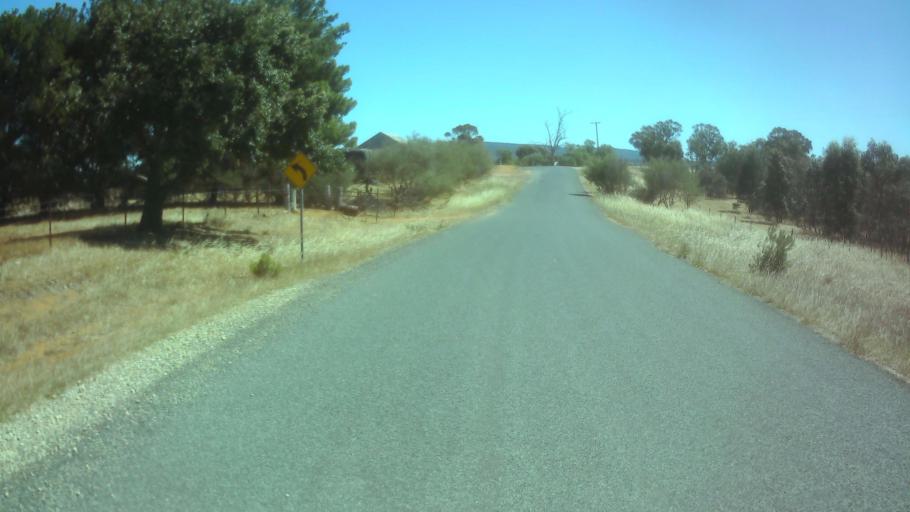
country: AU
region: New South Wales
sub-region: Weddin
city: Grenfell
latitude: -33.9549
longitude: 148.3989
